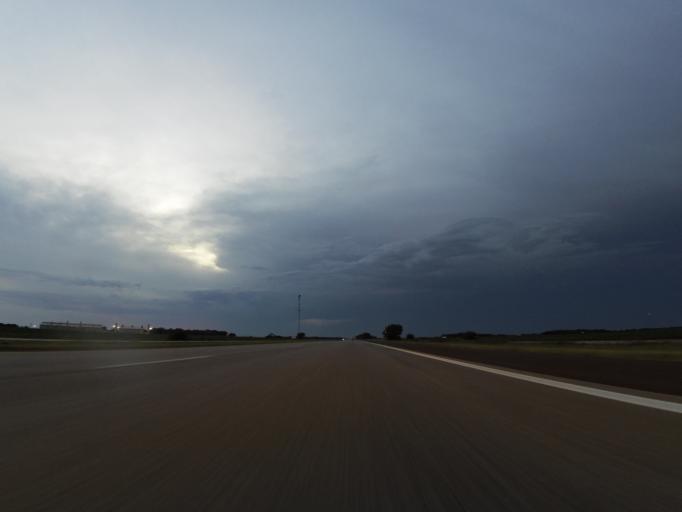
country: US
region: Kansas
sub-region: Reno County
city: Haven
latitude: 37.9072
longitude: -97.8026
